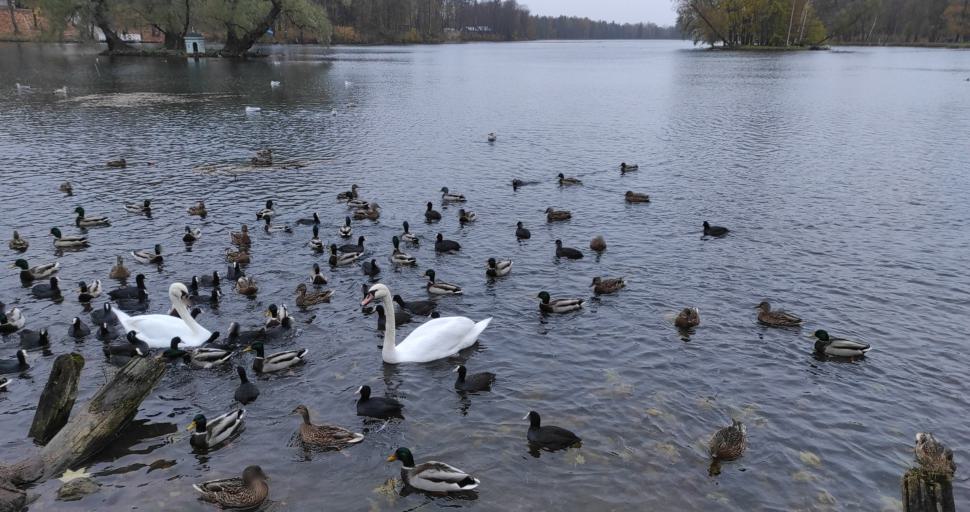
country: RU
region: Leningrad
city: Gatchina
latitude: 59.5638
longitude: 30.1151
